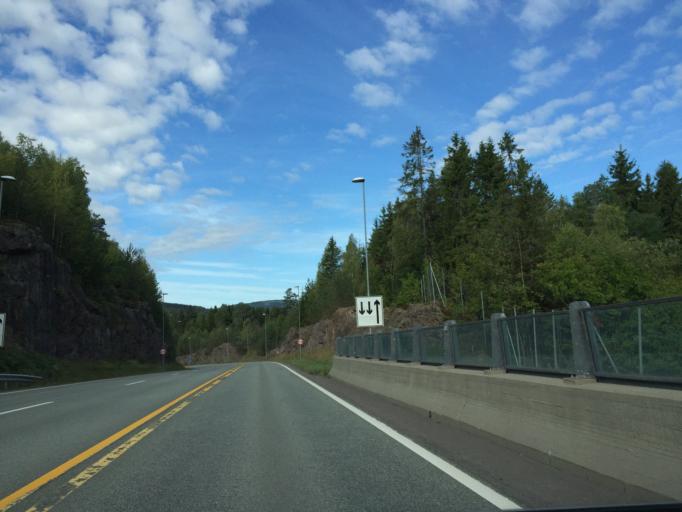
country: NO
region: Vestfold
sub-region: Holmestrand
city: Gullhaug
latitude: 59.5072
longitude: 10.1942
